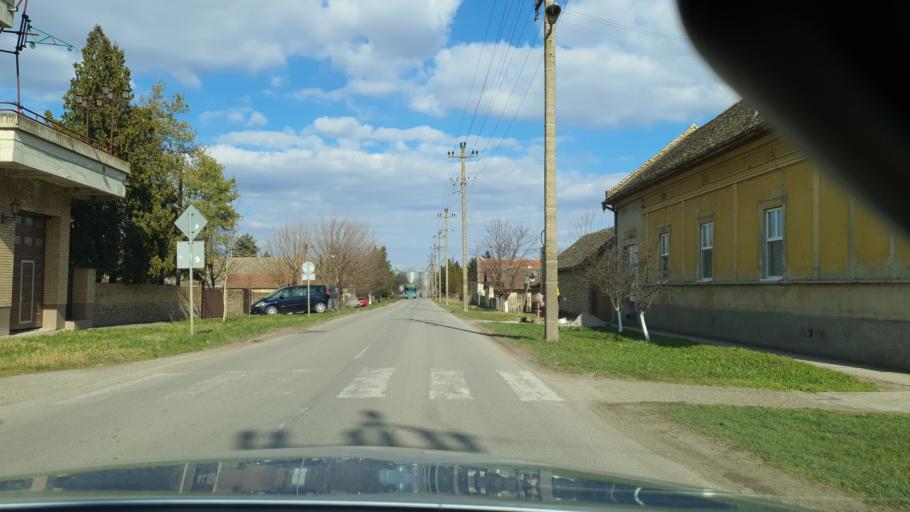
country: RS
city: Ravno Selo
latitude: 45.4492
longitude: 19.6280
